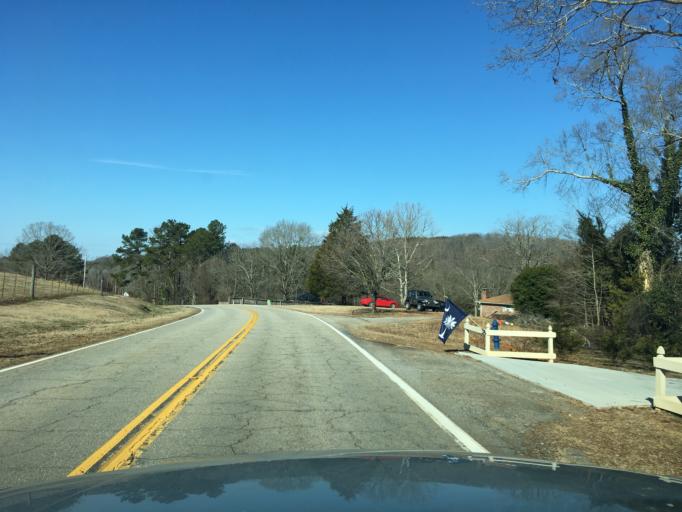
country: US
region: South Carolina
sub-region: Pickens County
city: Pickens
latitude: 34.8756
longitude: -82.6721
